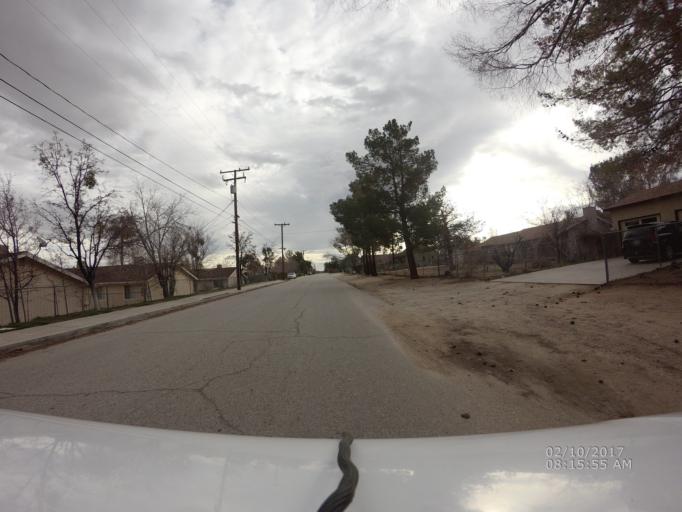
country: US
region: California
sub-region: Los Angeles County
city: Littlerock
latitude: 34.5047
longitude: -117.9094
